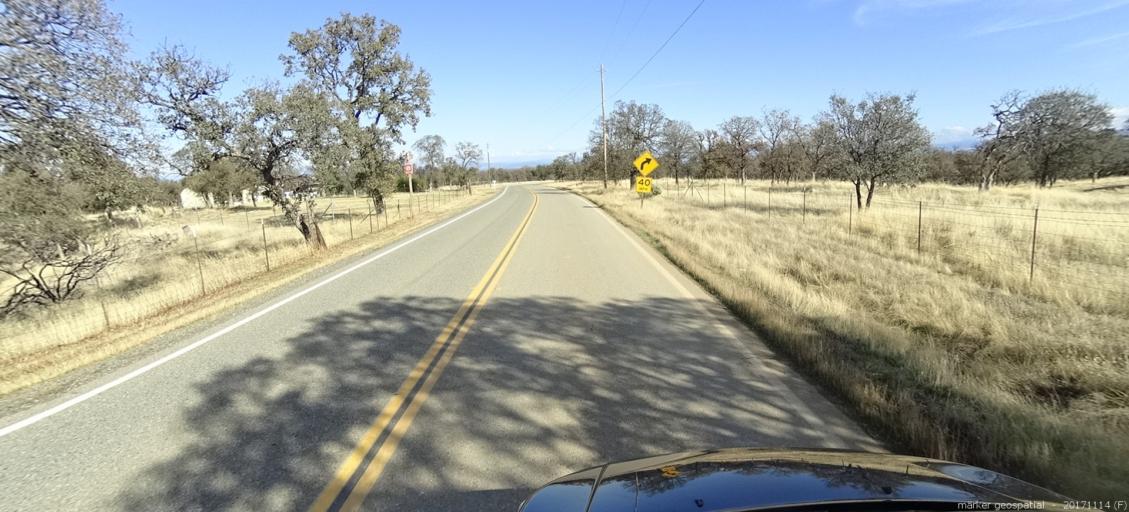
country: US
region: California
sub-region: Shasta County
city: Anderson
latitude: 40.4163
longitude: -122.3406
